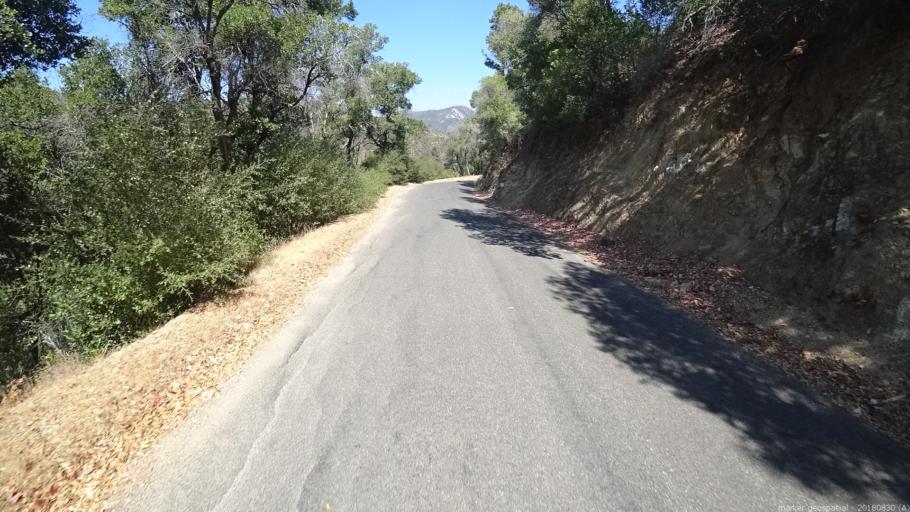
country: US
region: California
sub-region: Monterey County
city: Greenfield
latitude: 36.0132
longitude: -121.4408
